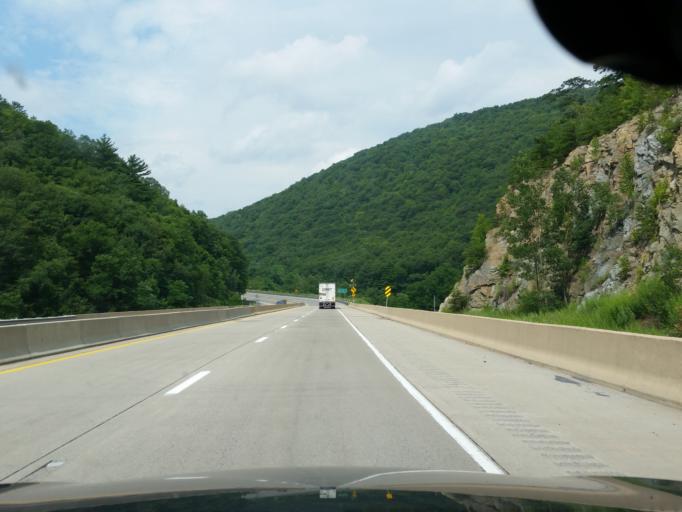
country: US
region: Pennsylvania
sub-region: Mifflin County
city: Milroy
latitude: 40.7312
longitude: -77.6119
